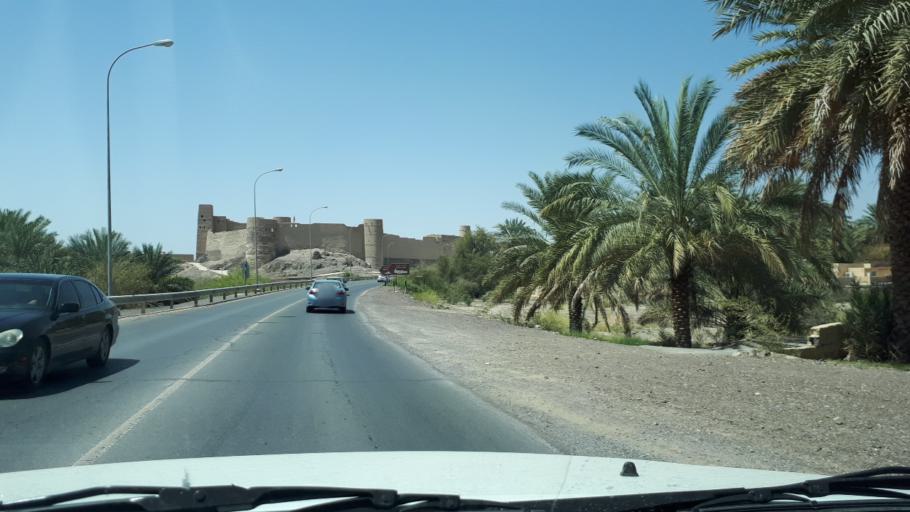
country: OM
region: Muhafazat ad Dakhiliyah
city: Bahla'
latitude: 22.9672
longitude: 57.3020
